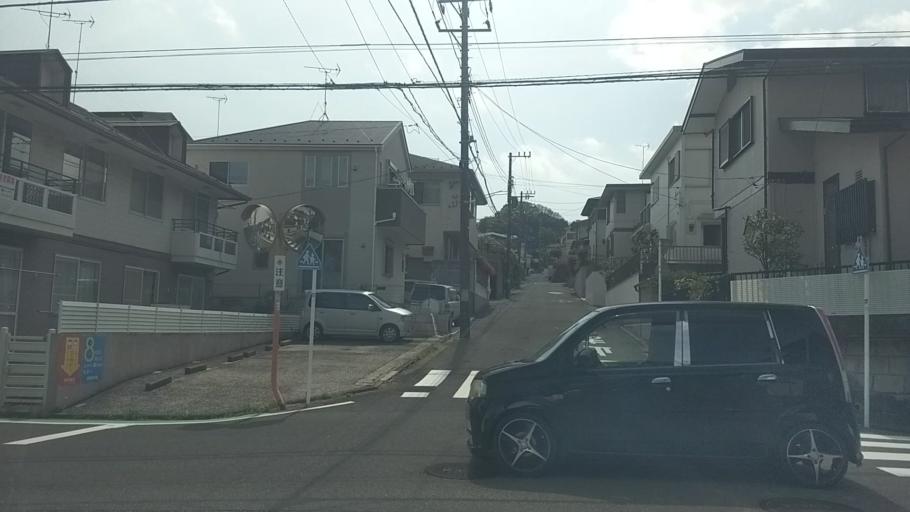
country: JP
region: Kanagawa
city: Yokohama
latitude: 35.3905
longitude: 139.5921
